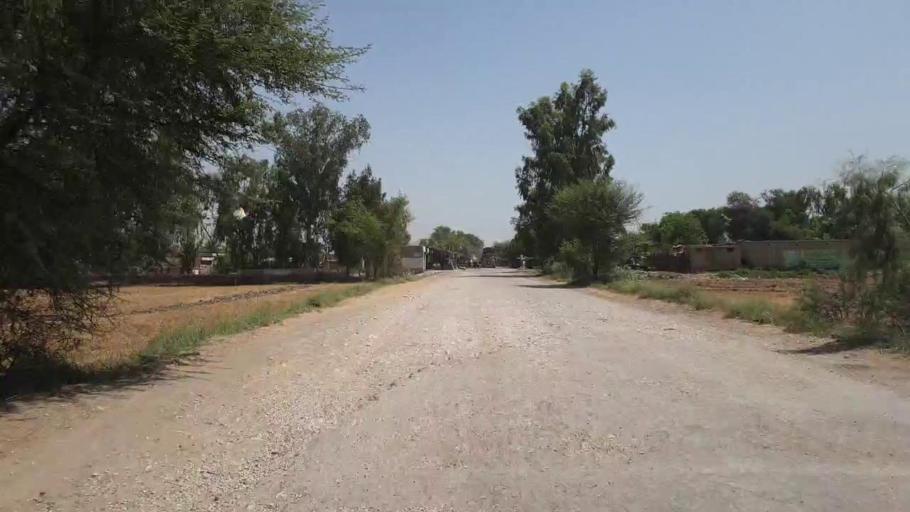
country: PK
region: Sindh
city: Adilpur
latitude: 27.8432
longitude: 69.2691
